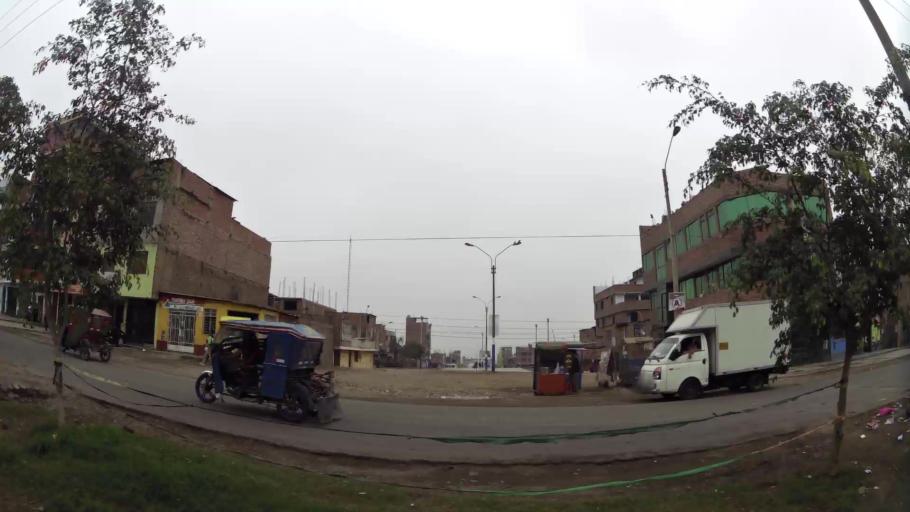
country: PE
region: Lima
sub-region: Lima
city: Independencia
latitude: -11.9459
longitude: -76.9788
